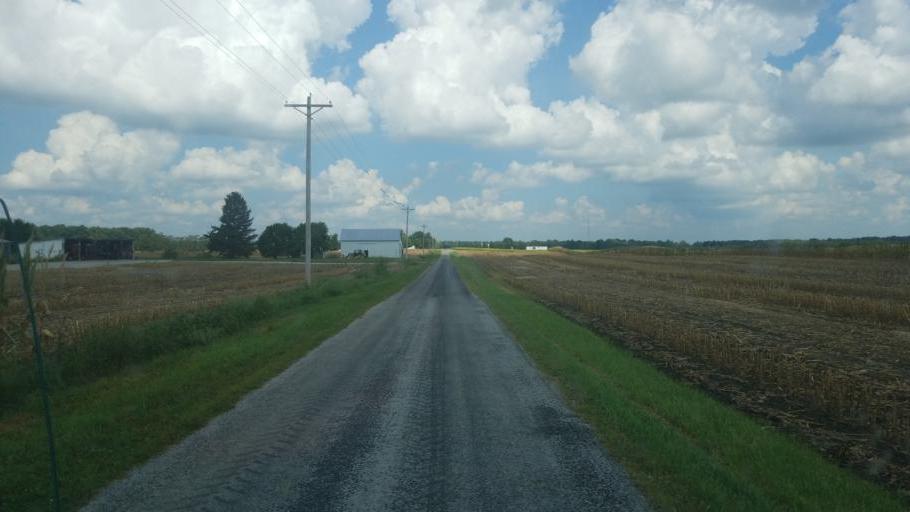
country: US
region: Ohio
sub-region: Hardin County
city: Kenton
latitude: 40.6927
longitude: -83.6385
